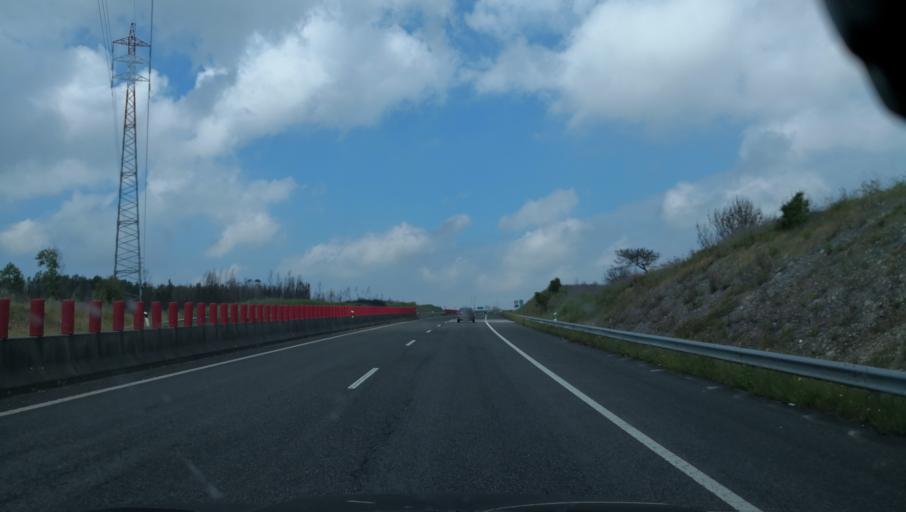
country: PT
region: Leiria
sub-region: Peniche
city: Atouguia da Baleia
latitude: 39.3317
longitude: -9.2483
